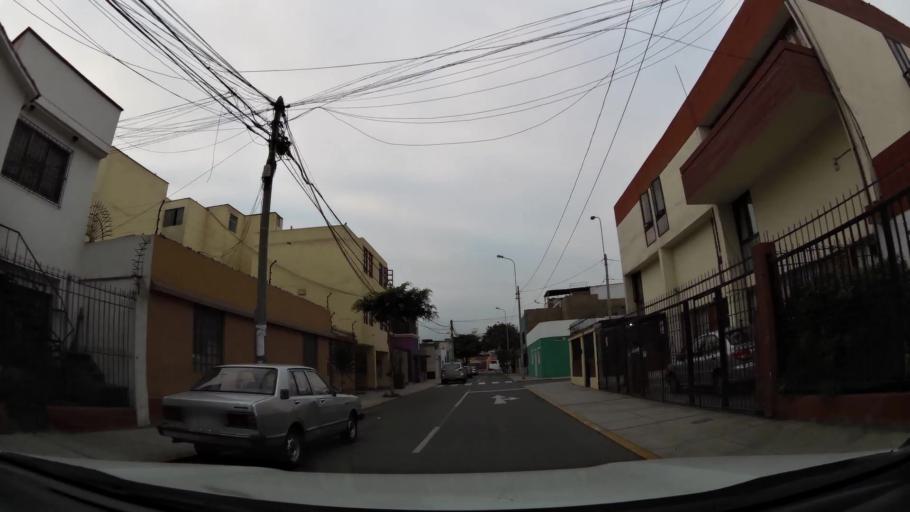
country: PE
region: Lima
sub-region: Lima
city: Surco
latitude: -12.1424
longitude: -77.0208
